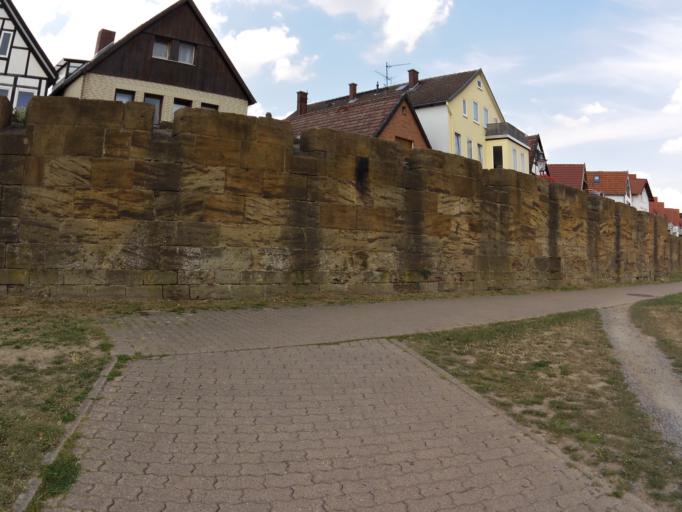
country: DE
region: North Rhine-Westphalia
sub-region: Regierungsbezirk Detmold
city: Minden
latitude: 52.2920
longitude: 8.9241
